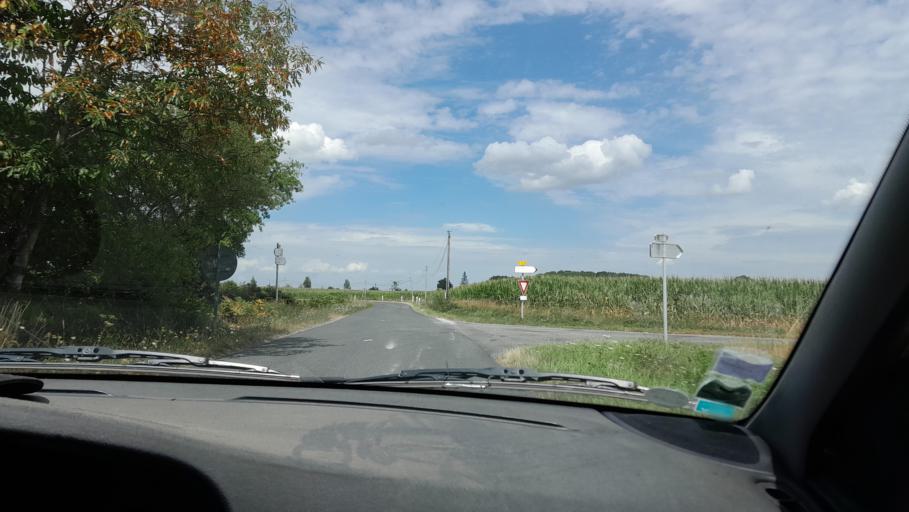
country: FR
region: Pays de la Loire
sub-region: Departement de la Mayenne
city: Saint-Pierre-la-Cour
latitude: 48.1371
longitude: -1.0250
